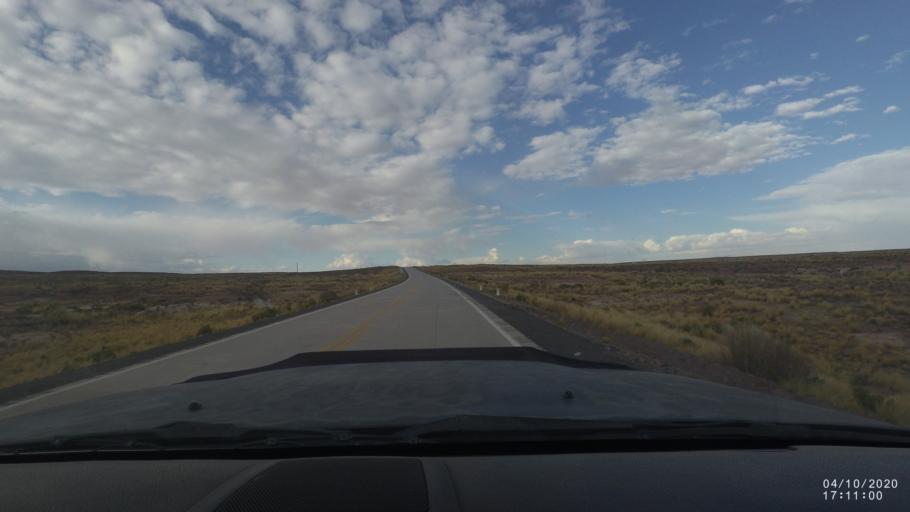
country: BO
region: Oruro
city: Oruro
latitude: -18.3247
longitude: -67.5794
